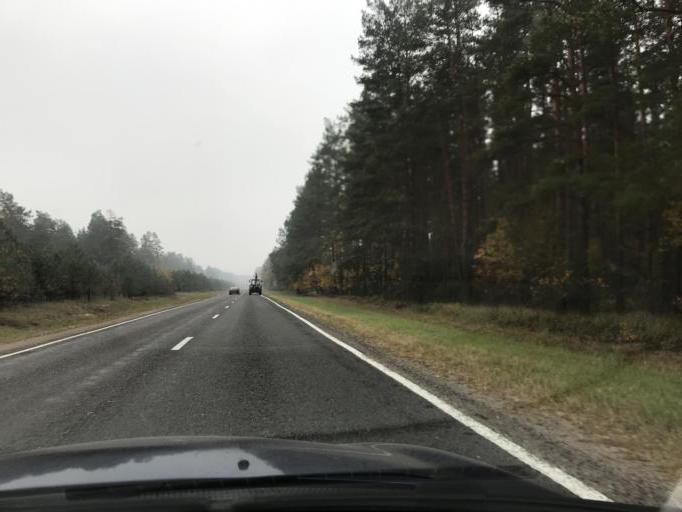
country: LT
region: Alytaus apskritis
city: Druskininkai
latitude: 53.8963
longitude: 23.9136
